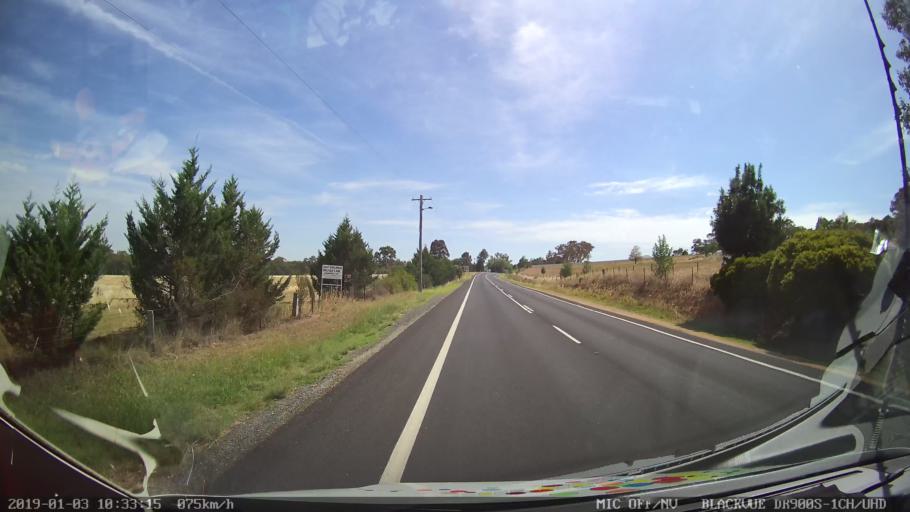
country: AU
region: New South Wales
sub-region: Young
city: Young
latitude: -34.3302
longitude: 148.2863
